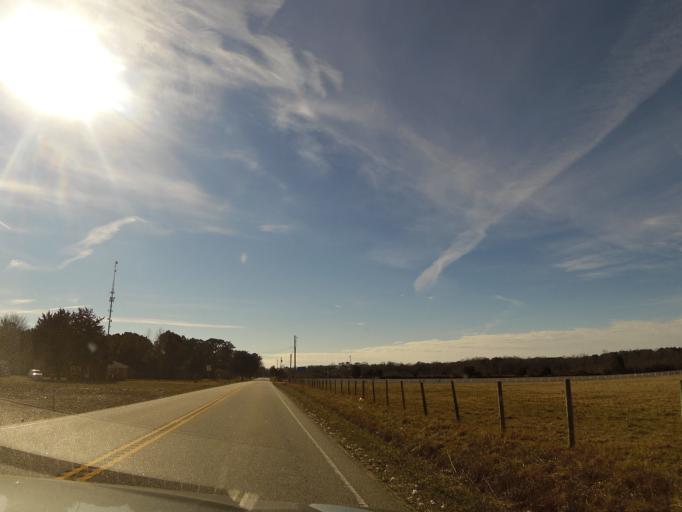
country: US
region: Virginia
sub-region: Isle of Wight County
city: Isle of Wight
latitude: 36.9133
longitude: -76.7004
